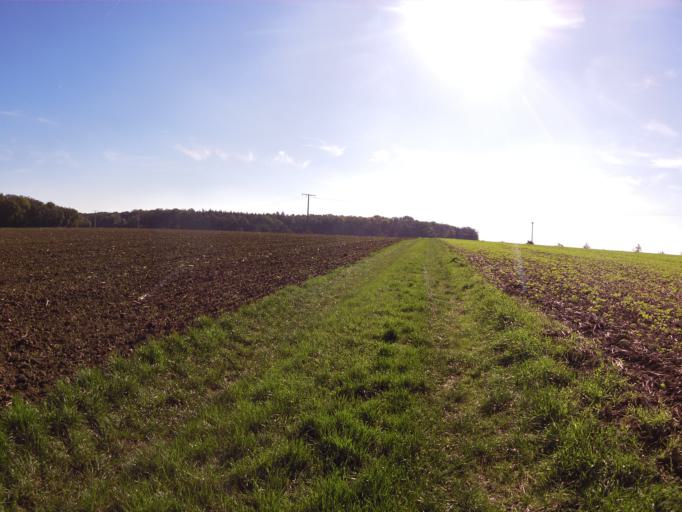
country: DE
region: Bavaria
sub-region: Regierungsbezirk Unterfranken
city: Frickenhausen
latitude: 49.7083
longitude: 10.0946
